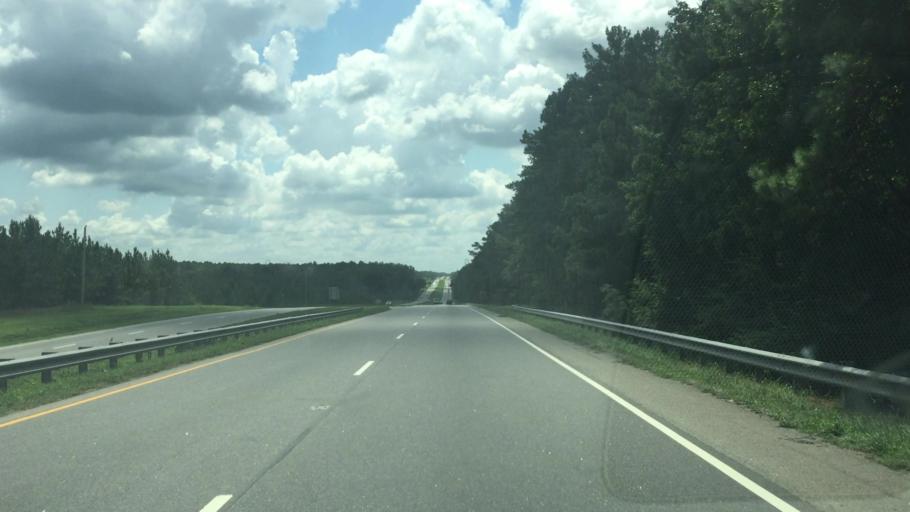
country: US
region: North Carolina
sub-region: Richmond County
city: Hamlet
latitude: 34.8614
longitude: -79.6335
